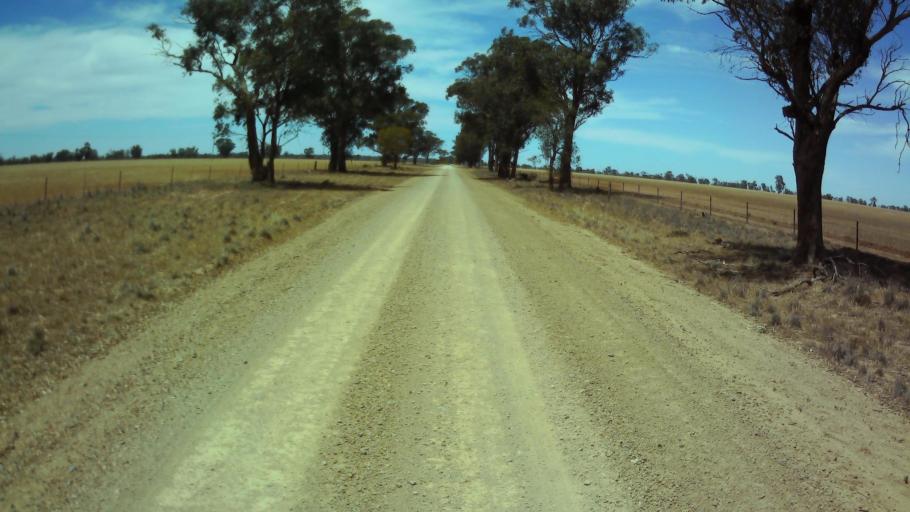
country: AU
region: New South Wales
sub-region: Weddin
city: Grenfell
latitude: -33.8720
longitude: 147.8061
